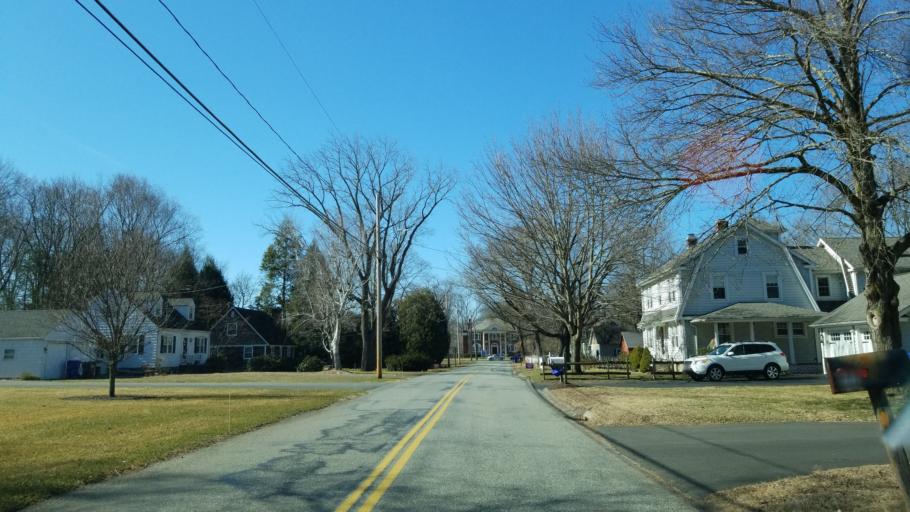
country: US
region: Connecticut
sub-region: Hartford County
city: South Windsor
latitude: 41.8227
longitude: -72.6189
